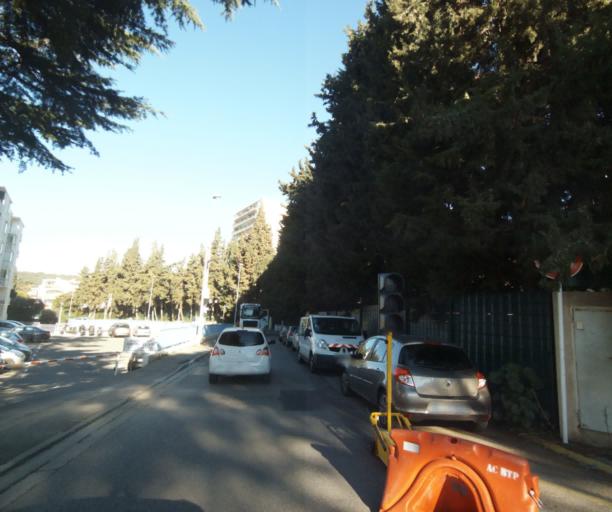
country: FR
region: Provence-Alpes-Cote d'Azur
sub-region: Departement des Alpes-Maritimes
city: Antibes
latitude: 43.5812
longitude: 7.0966
